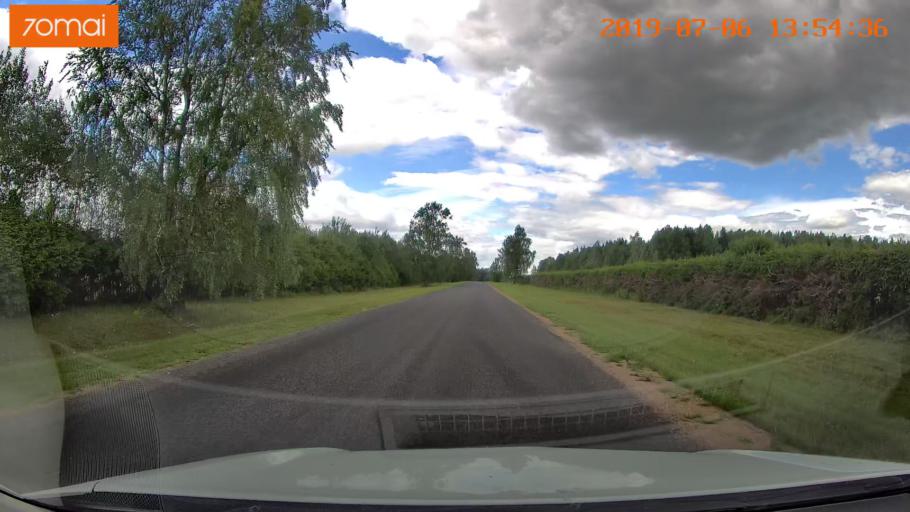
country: BY
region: Minsk
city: Ivyanyets
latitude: 53.7474
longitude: 26.8187
